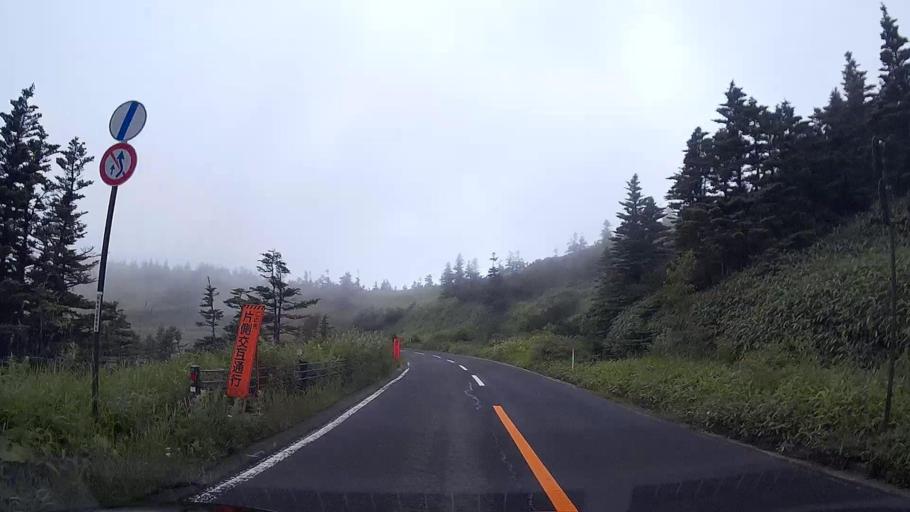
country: JP
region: Nagano
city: Nakano
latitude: 36.6577
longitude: 138.5307
